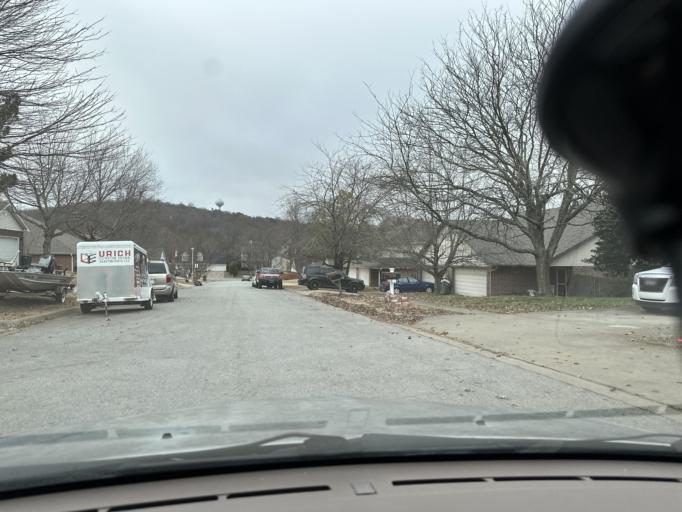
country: US
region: Arkansas
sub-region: Washington County
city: Fayetteville
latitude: 36.0854
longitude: -94.1185
